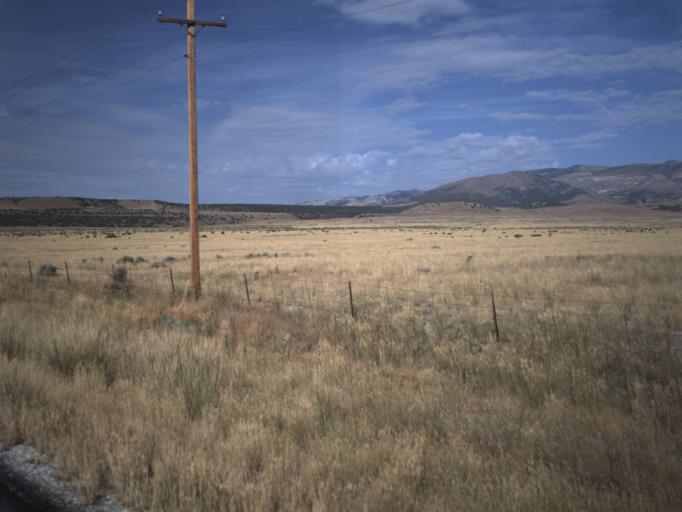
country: US
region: Idaho
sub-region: Minidoka County
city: Rupert
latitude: 41.8260
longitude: -113.1756
